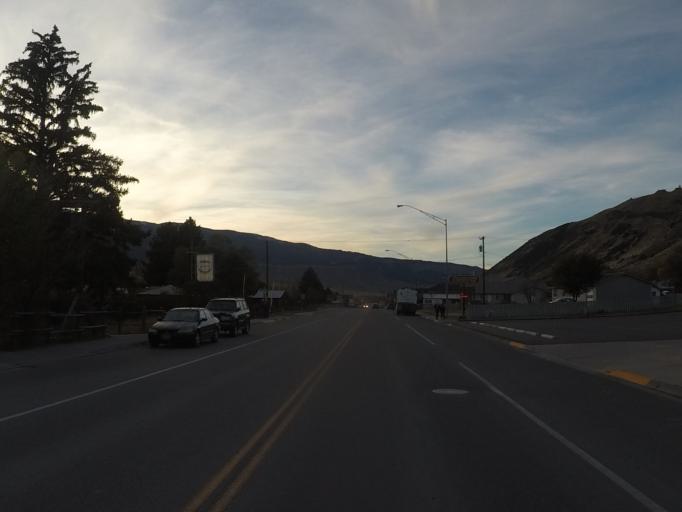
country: US
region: Montana
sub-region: Gallatin County
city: West Yellowstone
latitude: 45.0351
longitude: -110.7115
